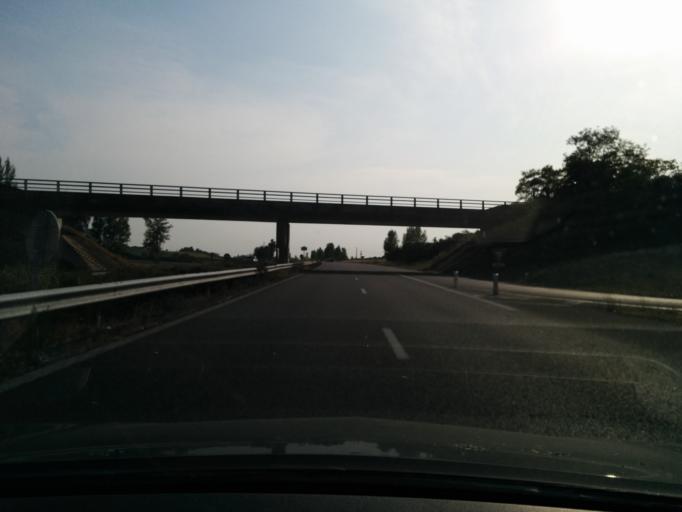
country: FR
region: Midi-Pyrenees
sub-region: Departement du Tarn
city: Lisle-sur-Tarn
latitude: 43.8413
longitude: 1.8462
